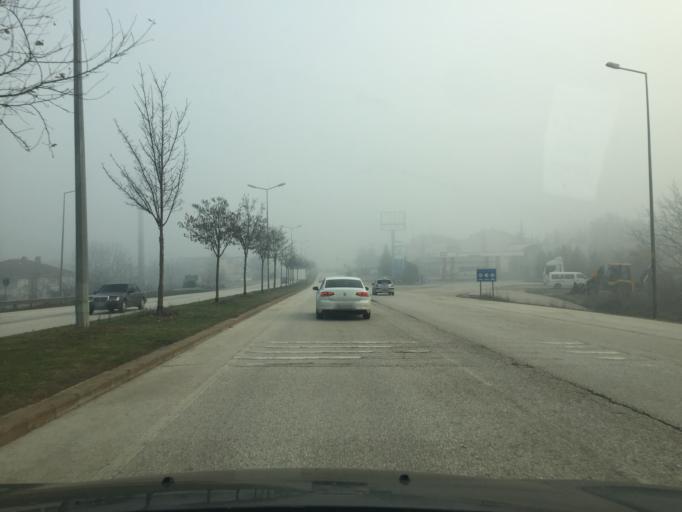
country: TR
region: Duzce
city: Duzce
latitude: 40.8388
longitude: 31.1762
